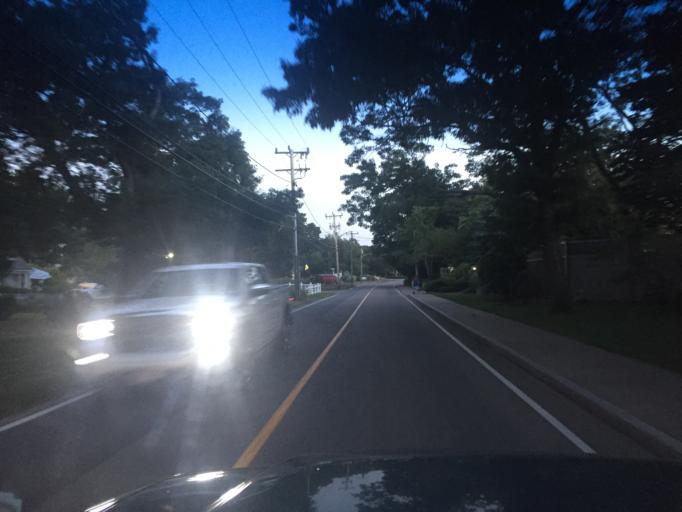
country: US
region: Massachusetts
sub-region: Barnstable County
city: Falmouth
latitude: 41.5486
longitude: -70.6005
